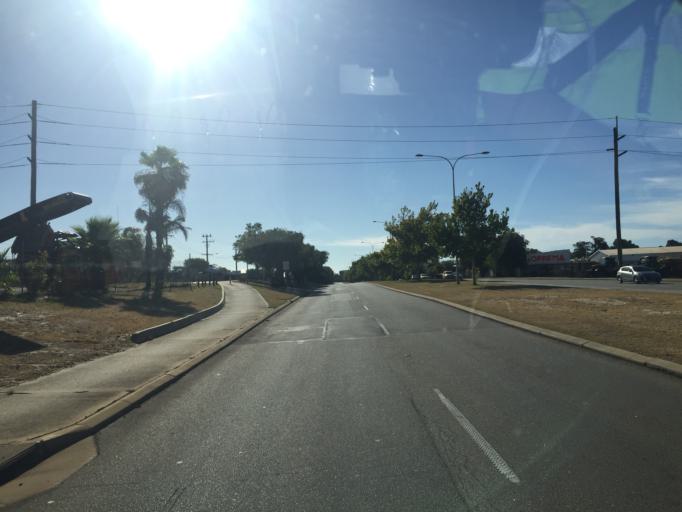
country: AU
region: Western Australia
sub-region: Canning
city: Queens Park
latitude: -31.9957
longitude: 115.9548
